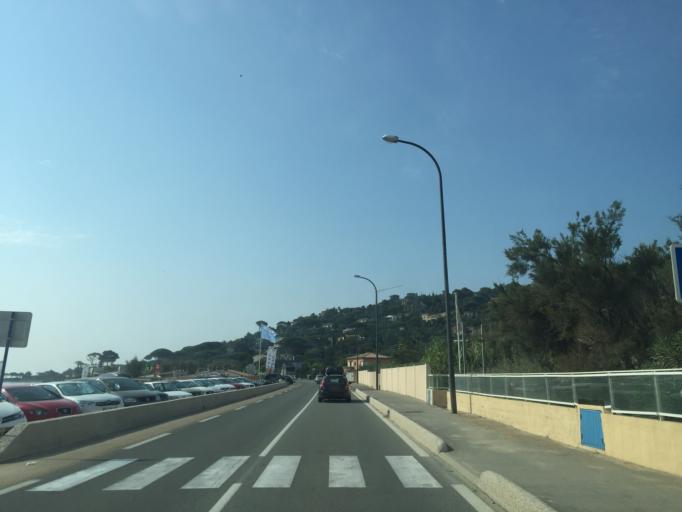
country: FR
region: Provence-Alpes-Cote d'Azur
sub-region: Departement du Var
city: Sainte-Maxime
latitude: 43.3197
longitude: 6.6648
